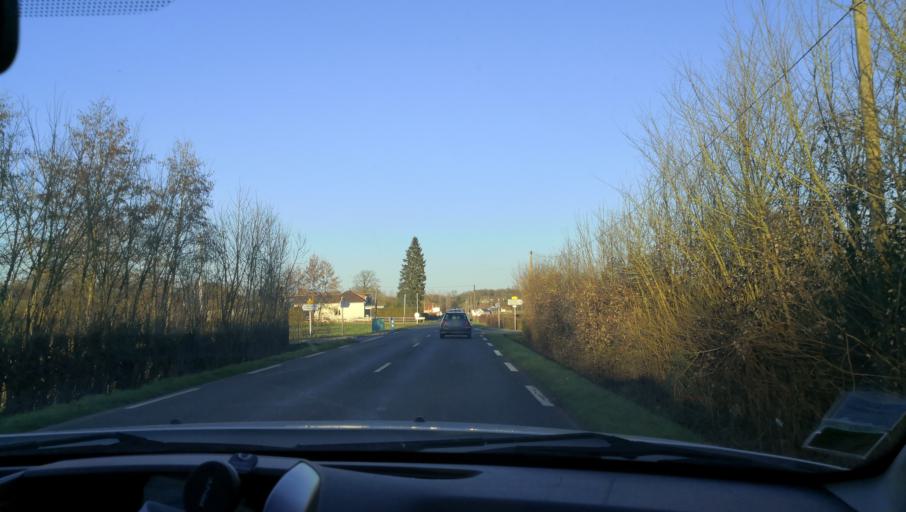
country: FR
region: Haute-Normandie
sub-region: Departement de la Seine-Maritime
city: Forges-les-Eaux
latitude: 49.6041
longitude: 1.4856
